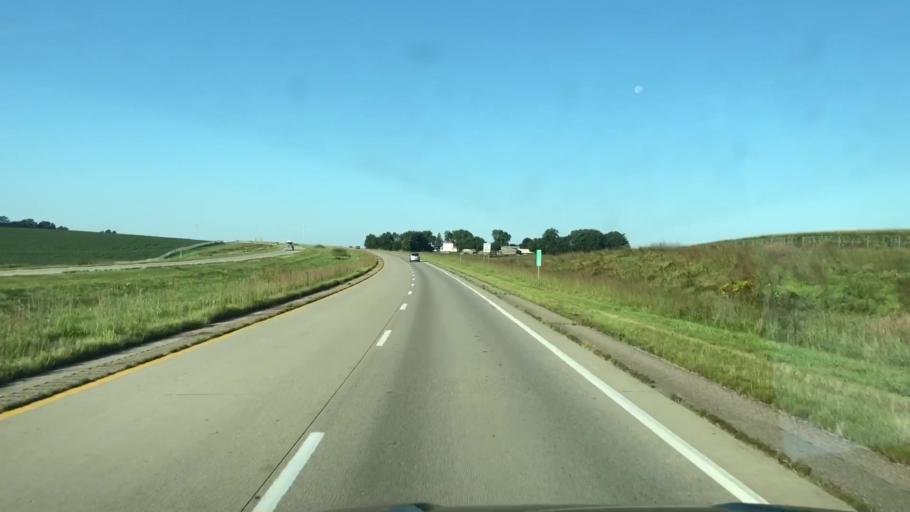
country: US
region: Iowa
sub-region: Plymouth County
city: Le Mars
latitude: 42.8163
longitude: -96.1864
